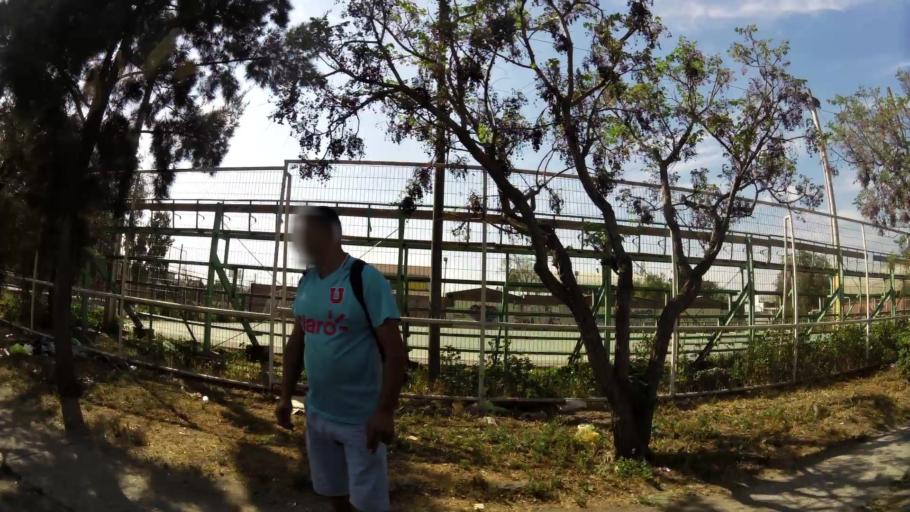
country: CL
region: Santiago Metropolitan
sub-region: Provincia de Santiago
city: La Pintana
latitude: -33.5596
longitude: -70.6671
